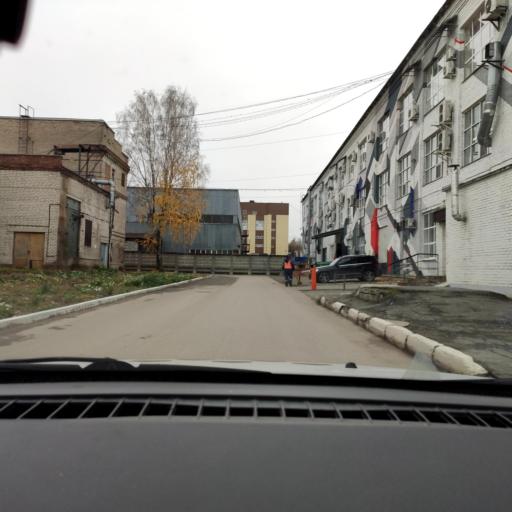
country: RU
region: Perm
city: Perm
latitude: 57.9909
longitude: 56.2059
